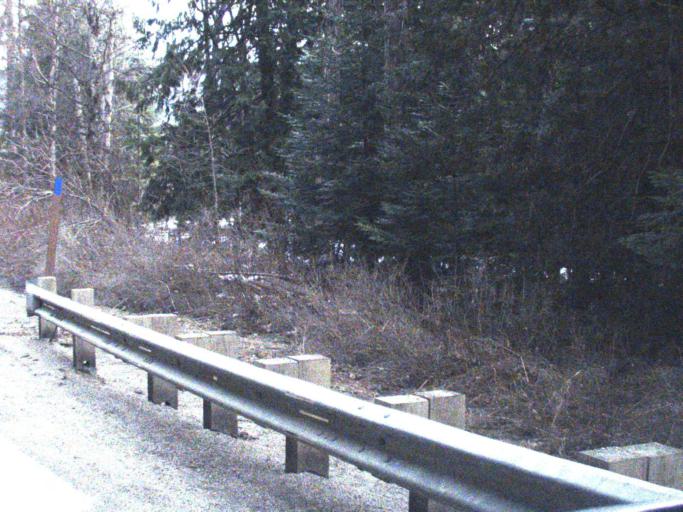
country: US
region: Washington
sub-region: Stevens County
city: Chewelah
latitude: 48.5675
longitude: -117.3546
